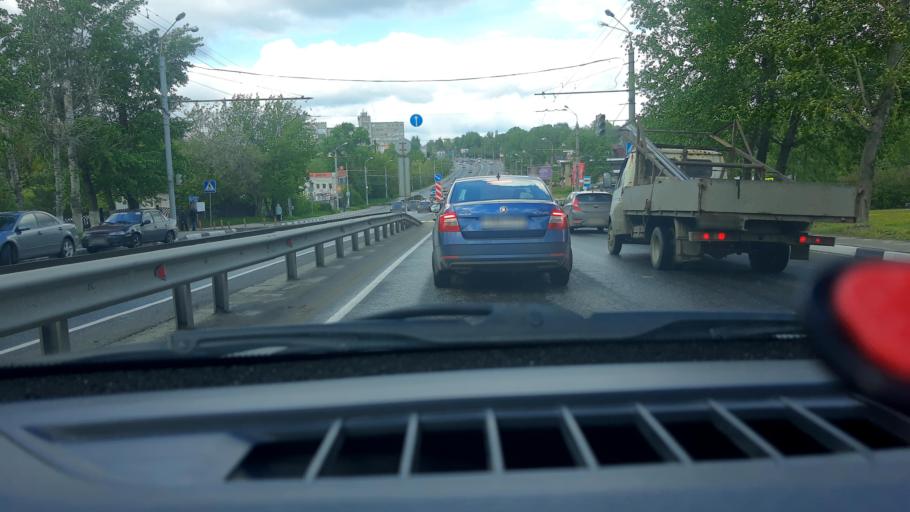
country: RU
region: Nizjnij Novgorod
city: Nizhniy Novgorod
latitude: 56.2868
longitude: 44.0335
